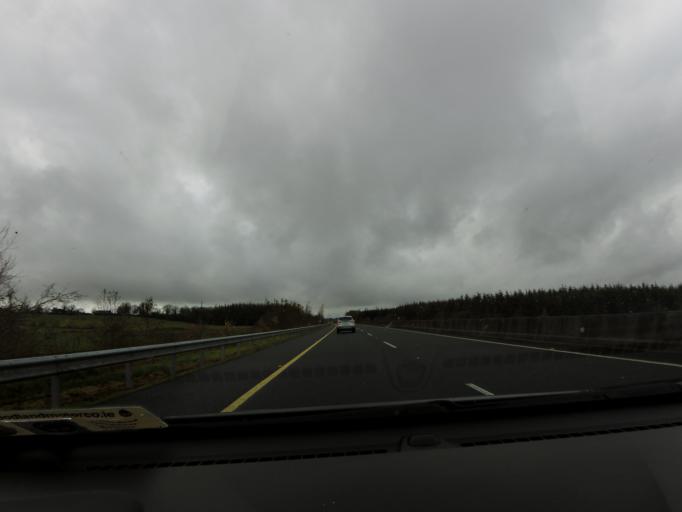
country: IE
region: Connaught
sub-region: County Galway
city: Loughrea
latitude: 53.2833
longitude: -8.4965
